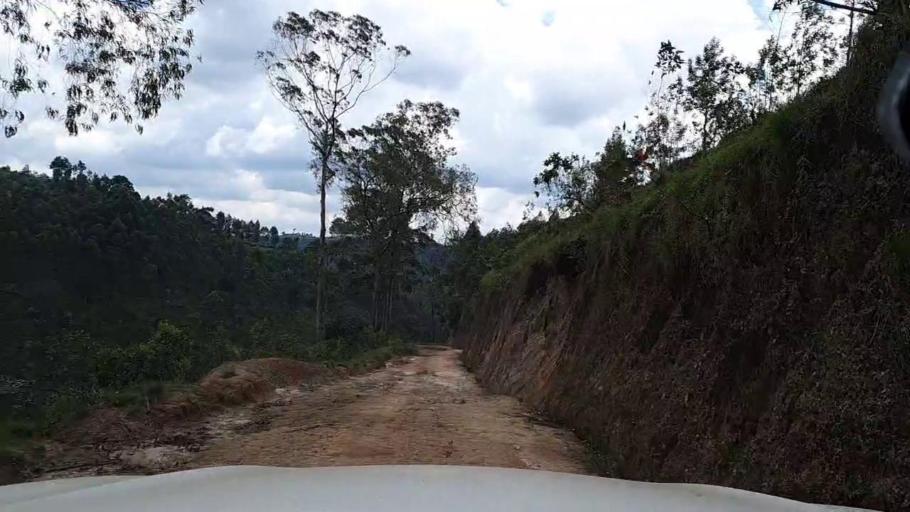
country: RW
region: Southern Province
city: Nzega
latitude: -2.6406
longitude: 29.4790
